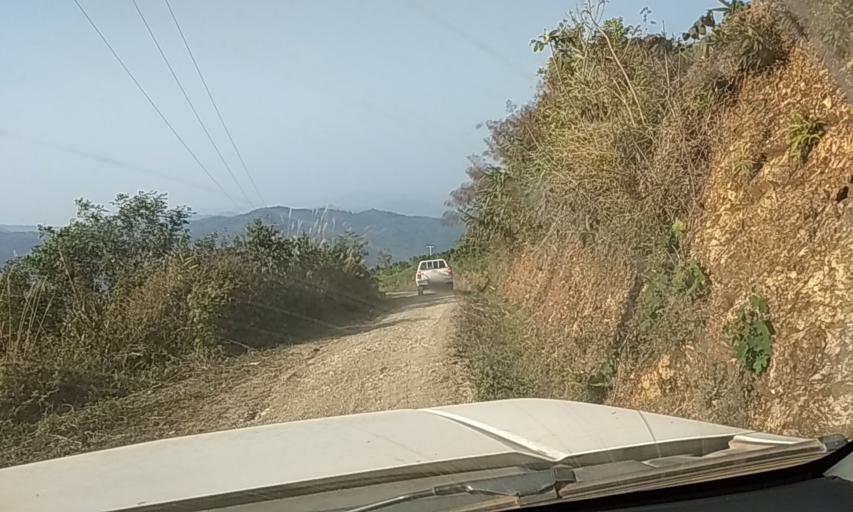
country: LA
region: Phongsali
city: Phongsali
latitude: 21.6656
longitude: 102.1799
